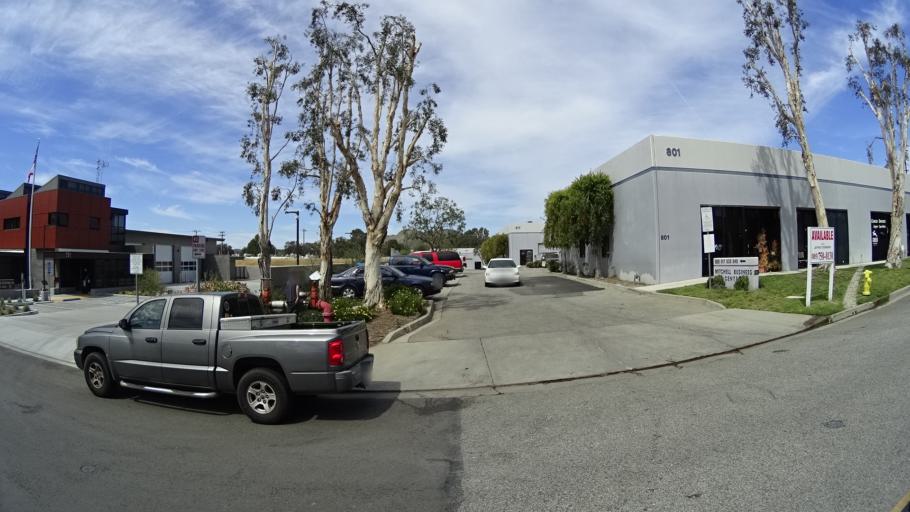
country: US
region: California
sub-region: Ventura County
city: Casa Conejo
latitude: 34.1889
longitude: -118.9268
